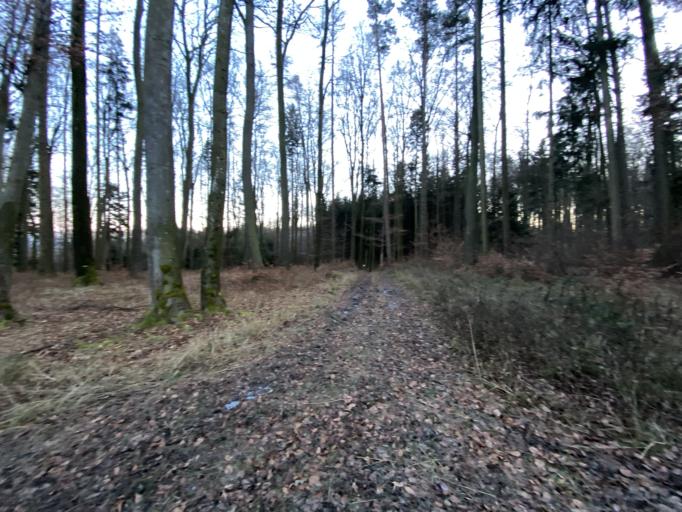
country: AT
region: Lower Austria
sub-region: Politischer Bezirk Sankt Polten
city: Boheimkirchen
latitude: 48.2095
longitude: 15.7275
